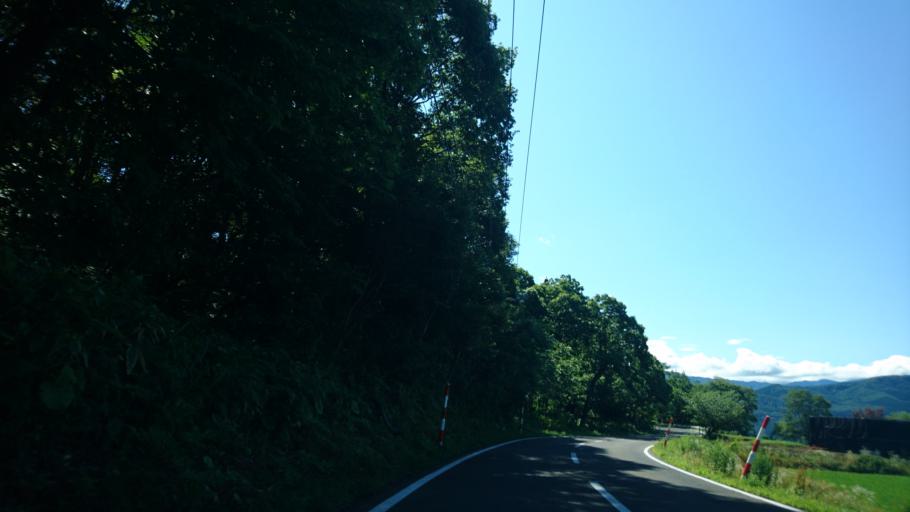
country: JP
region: Akita
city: Kakunodatemachi
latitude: 39.7479
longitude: 140.6781
